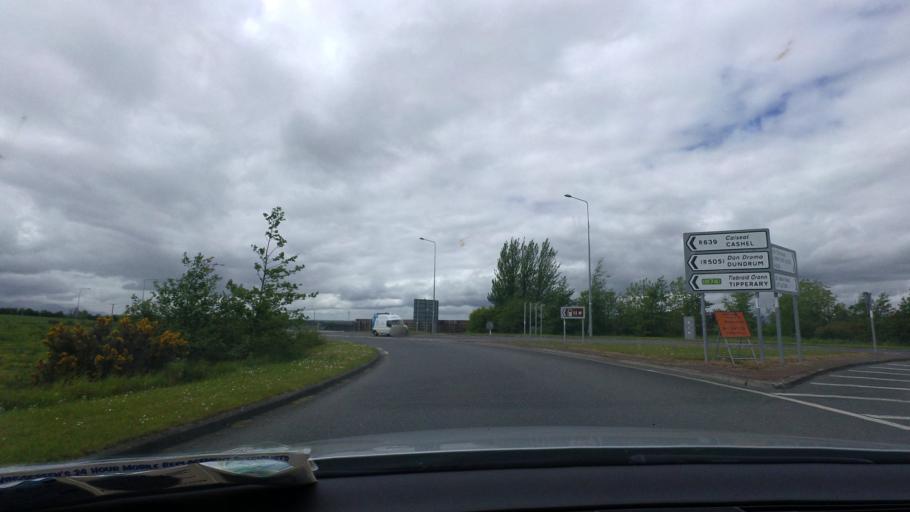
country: IE
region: Munster
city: Cashel
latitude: 52.5427
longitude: -7.8668
